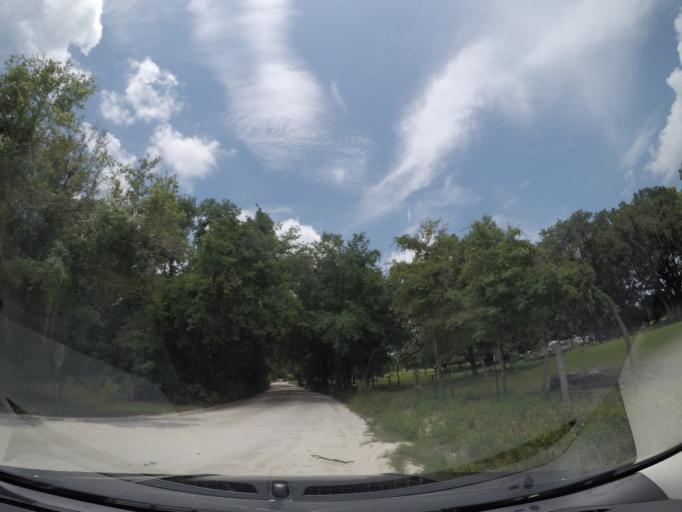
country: US
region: Florida
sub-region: Alachua County
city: High Springs
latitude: 29.8309
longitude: -82.7083
